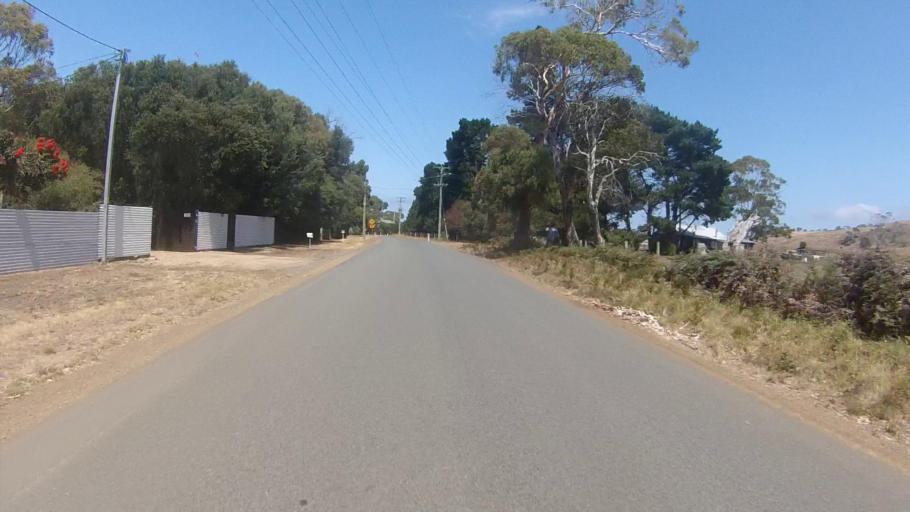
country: AU
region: Tasmania
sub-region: Sorell
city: Sorell
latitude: -42.8238
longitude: 147.8593
